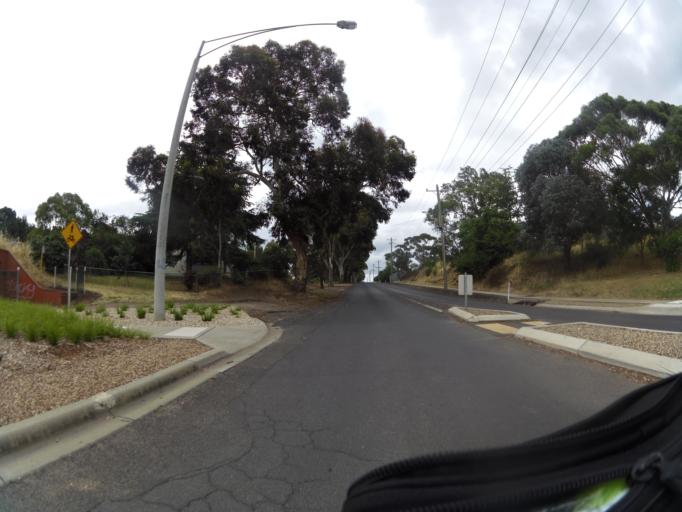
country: AU
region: Victoria
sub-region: Mount Alexander
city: Castlemaine
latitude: -37.0664
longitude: 144.2140
